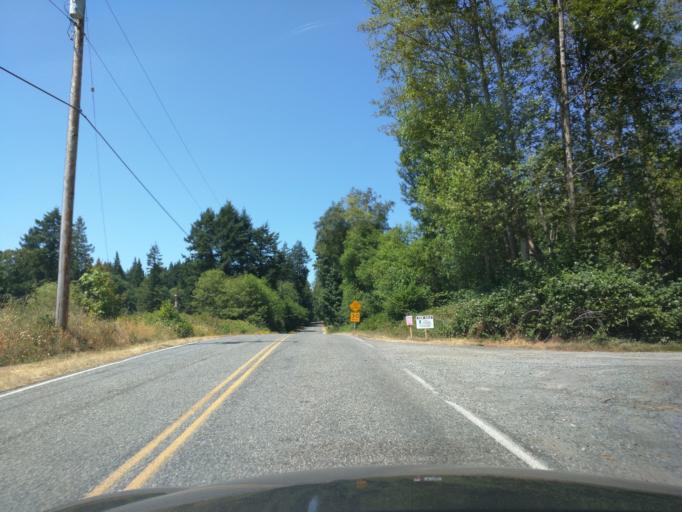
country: US
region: Washington
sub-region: Whatcom County
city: Blaine
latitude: 48.9936
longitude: -122.6611
